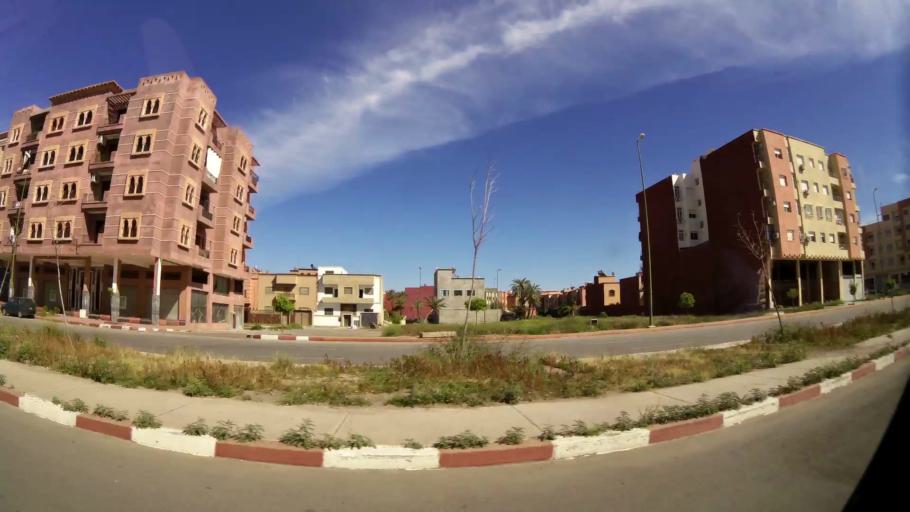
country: MA
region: Marrakech-Tensift-Al Haouz
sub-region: Marrakech
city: Marrakesh
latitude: 31.6690
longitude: -8.0298
